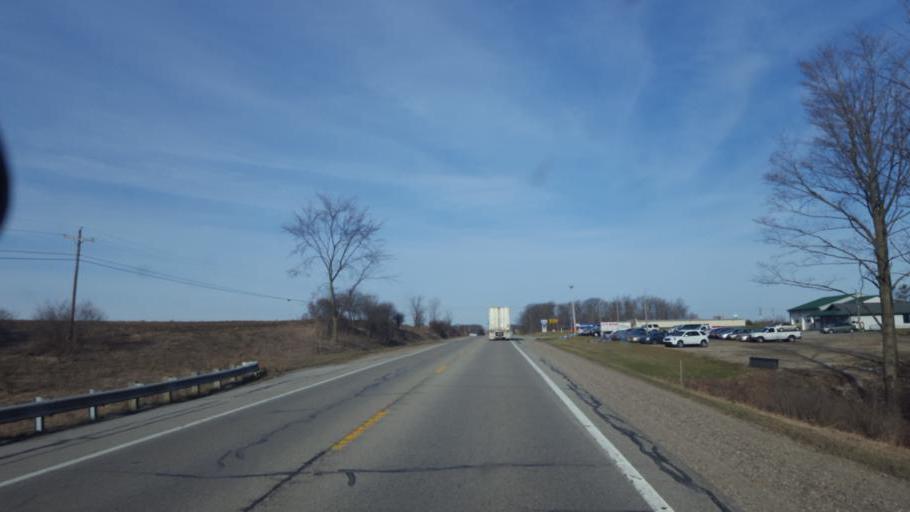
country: US
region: Michigan
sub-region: Montcalm County
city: Lakeview
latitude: 43.4314
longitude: -85.2535
